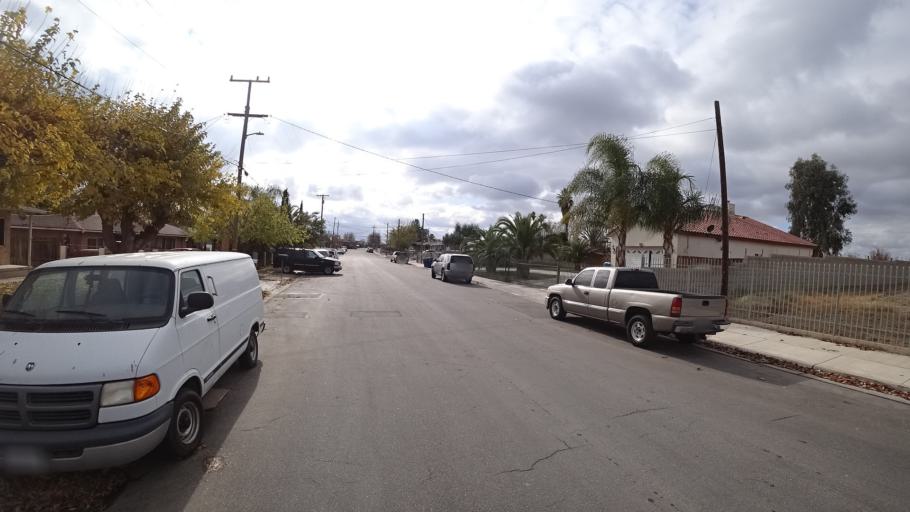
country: US
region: California
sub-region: Kern County
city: Bakersfield
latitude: 35.3338
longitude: -118.9910
